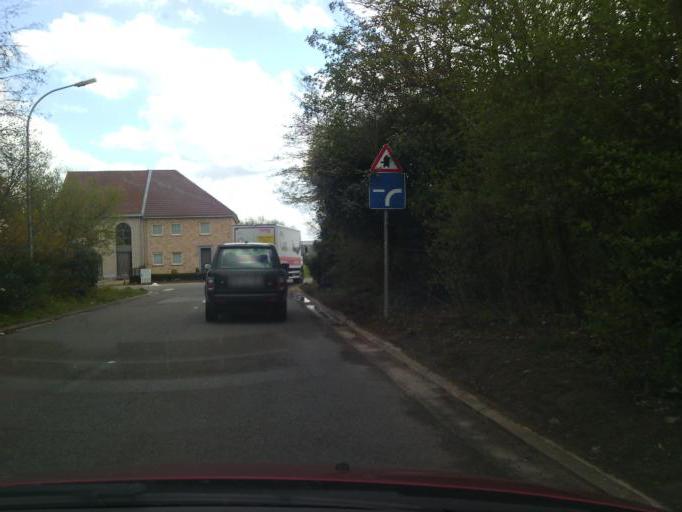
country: BE
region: Flanders
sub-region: Provincie Oost-Vlaanderen
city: Sint-Niklaas
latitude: 51.1464
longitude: 4.1736
